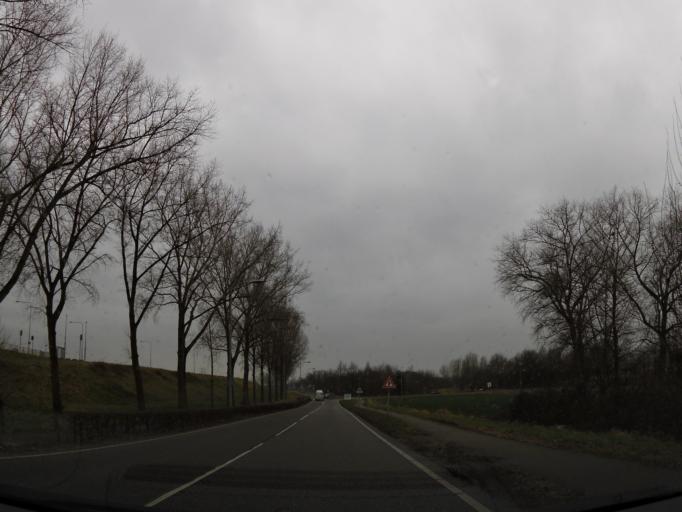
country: NL
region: Limburg
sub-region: Gemeente Maasgouw
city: Maasbracht
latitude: 51.1423
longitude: 5.8767
